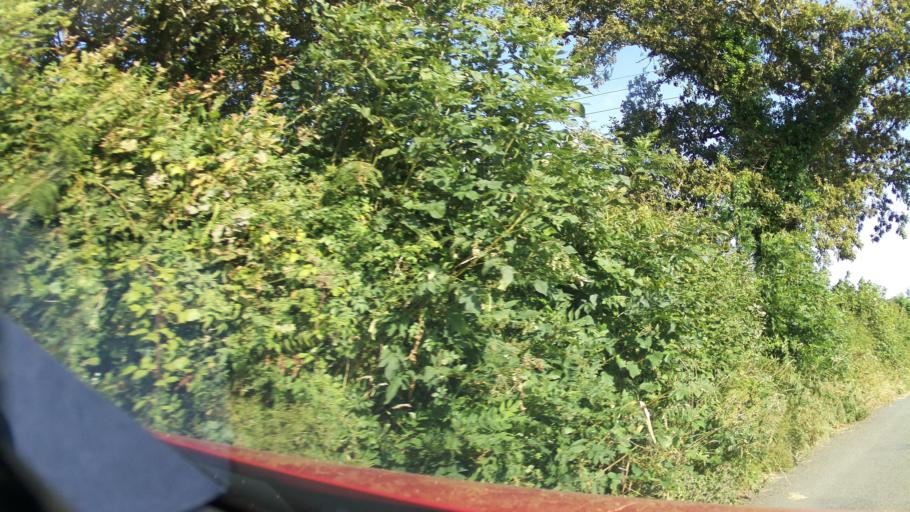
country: GB
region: England
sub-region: Devon
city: Buckfastleigh
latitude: 50.4342
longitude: -3.7745
